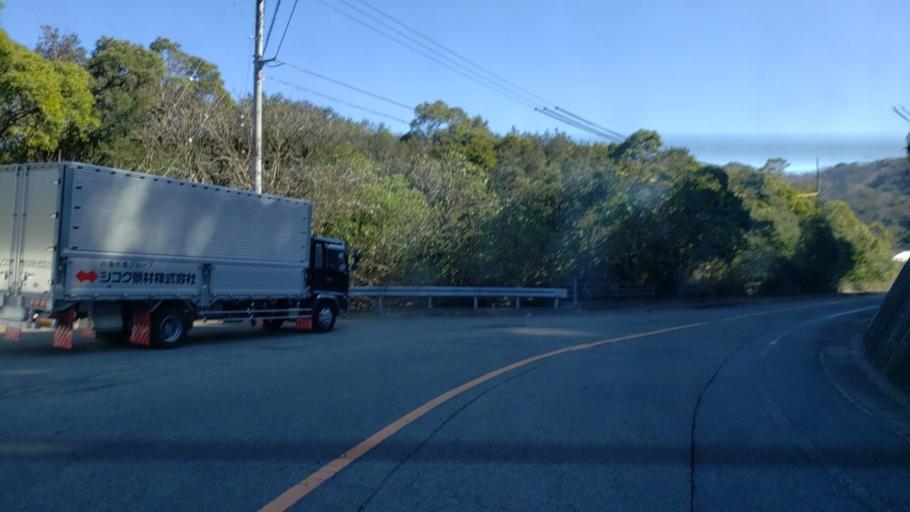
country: JP
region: Tokushima
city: Narutocho-mitsuishi
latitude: 34.2213
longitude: 134.5728
